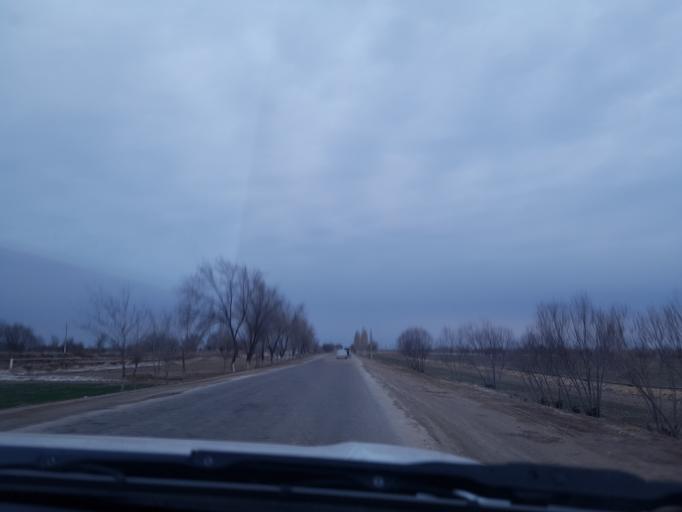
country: TM
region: Dasoguz
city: Yylanly
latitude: 41.9510
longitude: 59.5221
